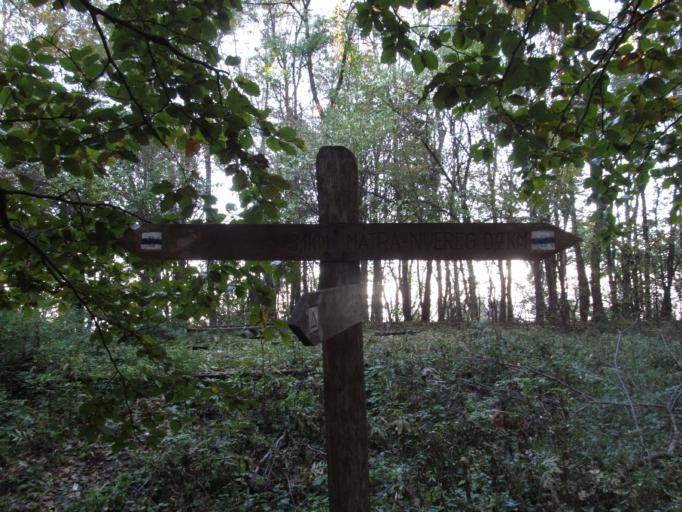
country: HU
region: Heves
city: Paradsasvar
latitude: 47.8935
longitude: 19.9700
